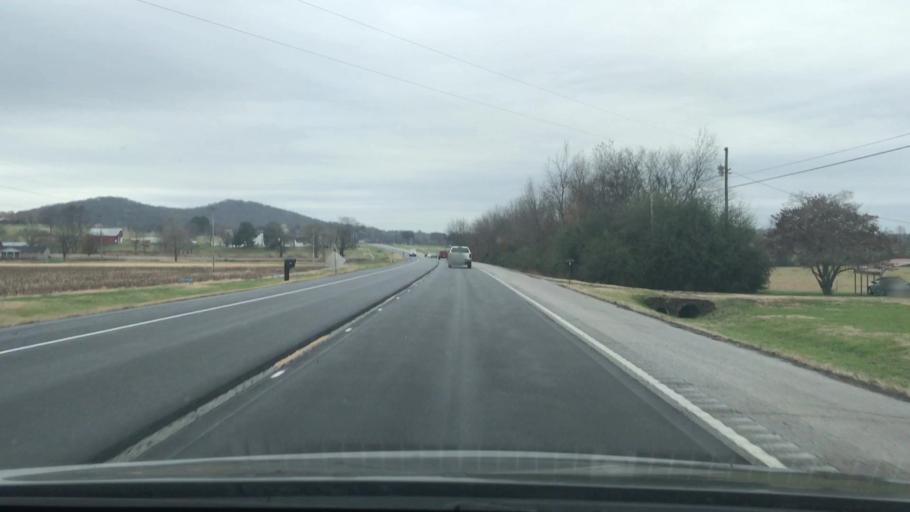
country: US
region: Tennessee
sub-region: Smith County
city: Carthage
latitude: 36.3446
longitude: -86.0361
